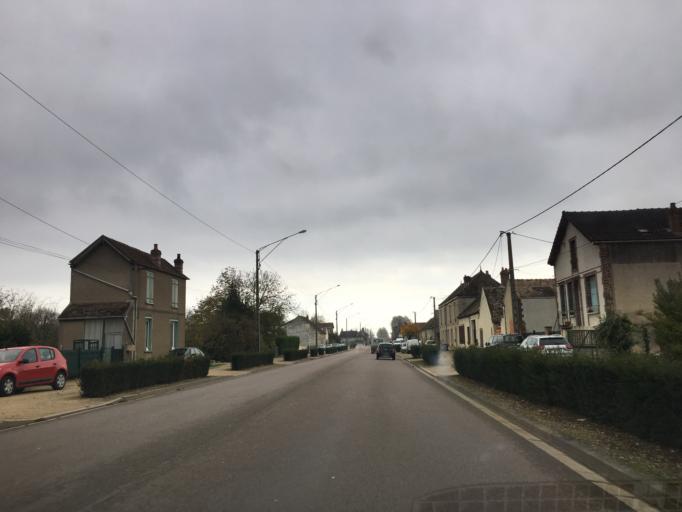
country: FR
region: Bourgogne
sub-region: Departement de l'Yonne
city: Champigny
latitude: 48.3249
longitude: 3.1249
